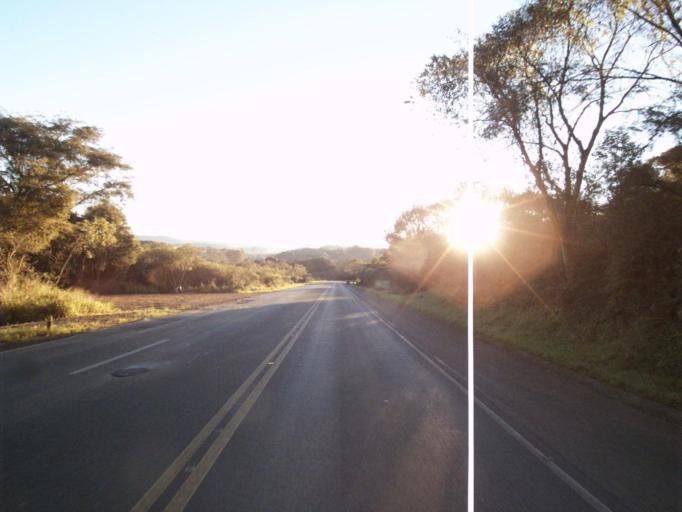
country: BR
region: Santa Catarina
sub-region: Sao Lourenco Do Oeste
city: Sao Lourenco dOeste
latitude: -26.8266
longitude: -53.0993
